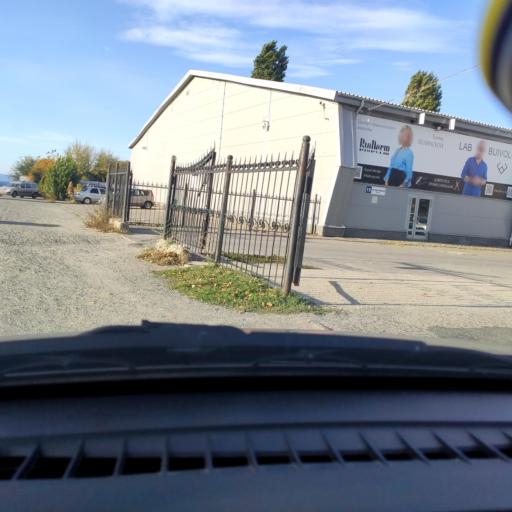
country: RU
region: Samara
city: Tol'yatti
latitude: 53.5012
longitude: 49.2609
